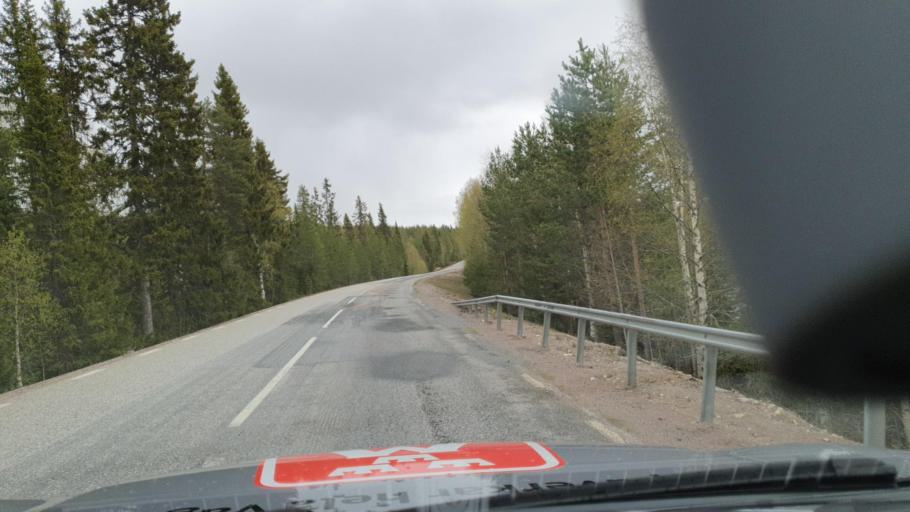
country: SE
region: Vaesternorrland
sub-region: Solleftea Kommun
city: Solleftea
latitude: 63.6543
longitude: 17.2973
